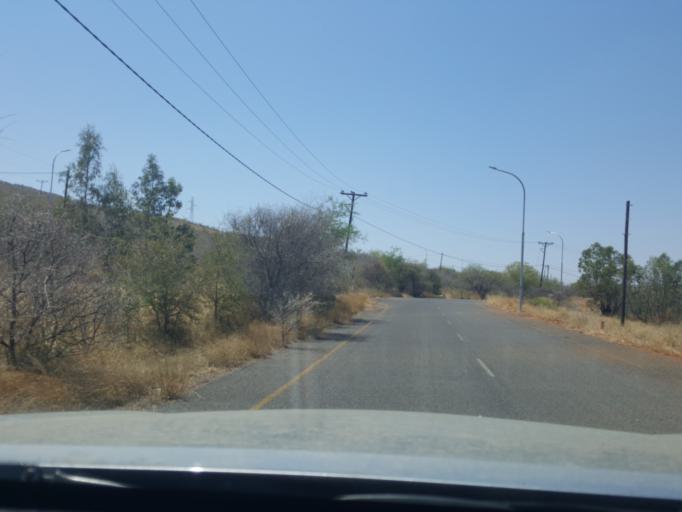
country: BW
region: South East
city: Lobatse
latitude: -25.1892
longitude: 25.6767
